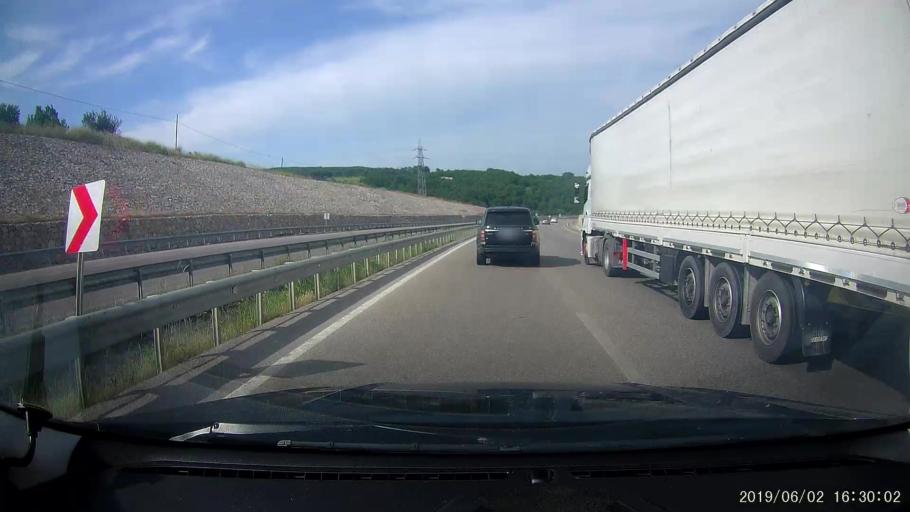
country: TR
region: Samsun
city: Ladik
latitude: 41.0216
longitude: 35.8746
